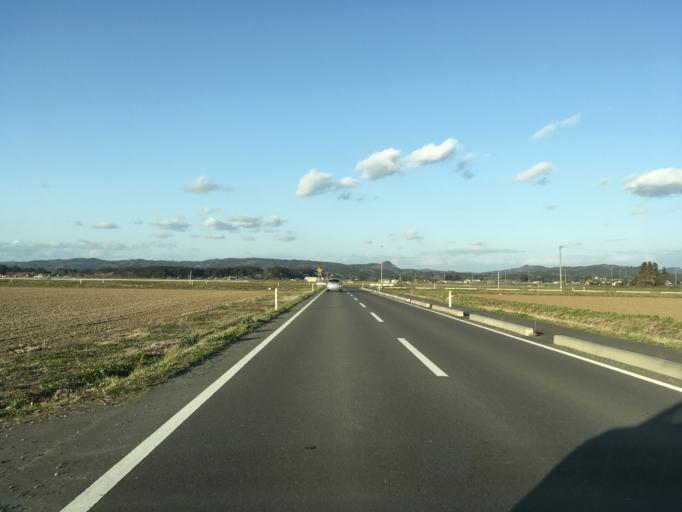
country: JP
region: Miyagi
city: Wakuya
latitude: 38.7223
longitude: 141.2389
